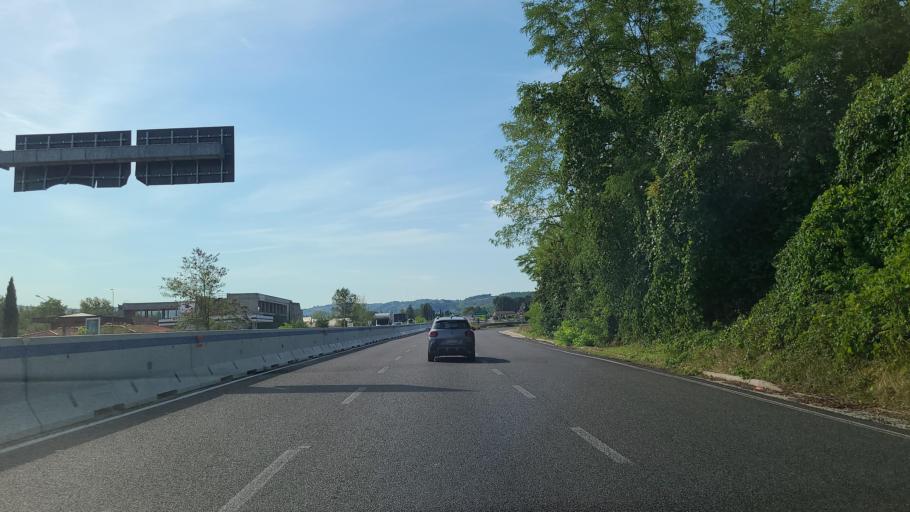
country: IT
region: Tuscany
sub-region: Province of Florence
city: Sambuca
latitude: 43.5928
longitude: 11.1988
